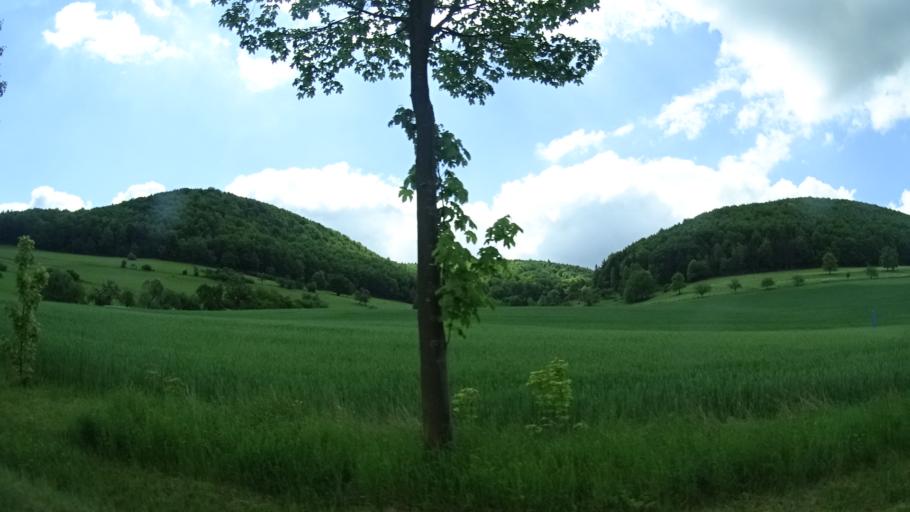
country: DE
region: Thuringia
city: Belrieth
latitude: 50.5259
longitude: 10.4909
